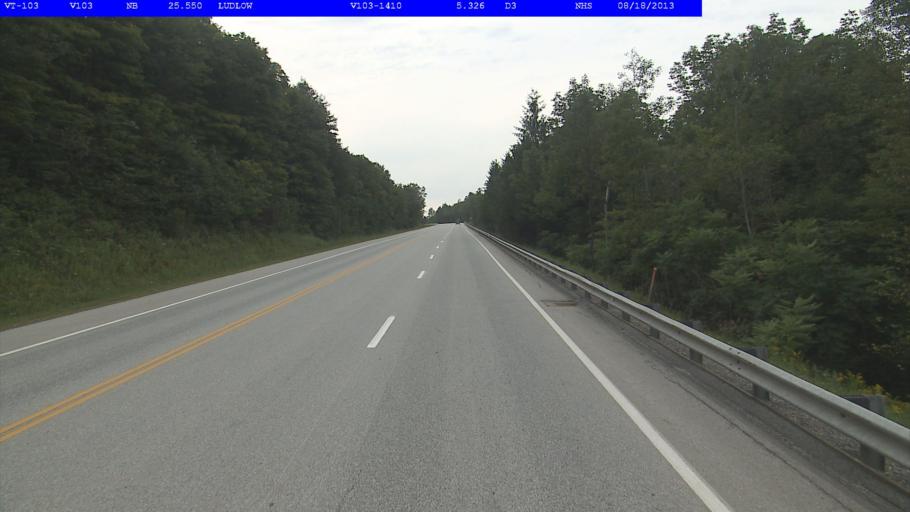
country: US
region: Vermont
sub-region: Windsor County
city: Chester
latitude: 43.4330
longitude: -72.7245
